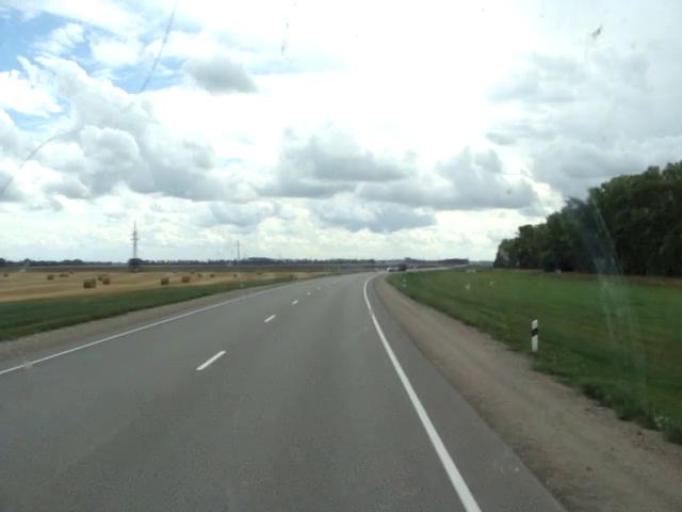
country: RU
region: Altai Krai
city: Shubenka
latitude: 52.6799
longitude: 85.0487
